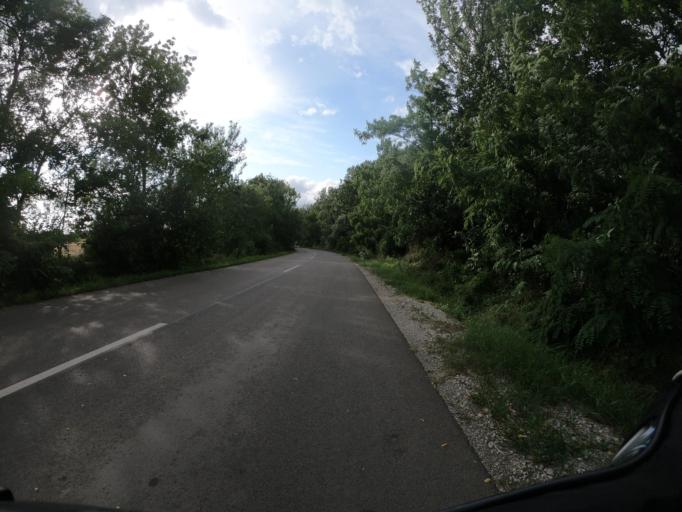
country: HU
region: Borsod-Abauj-Zemplen
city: Mezocsat
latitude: 47.8261
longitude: 20.8490
